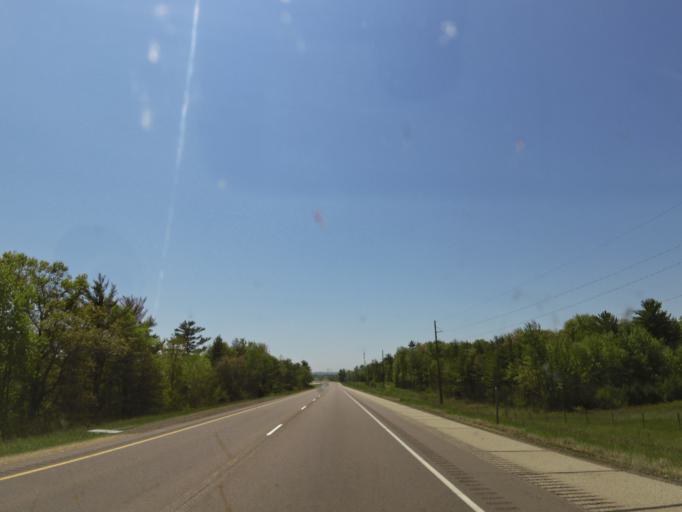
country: US
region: Wisconsin
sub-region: Monroe County
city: Tomah
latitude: 44.0349
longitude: -90.5135
